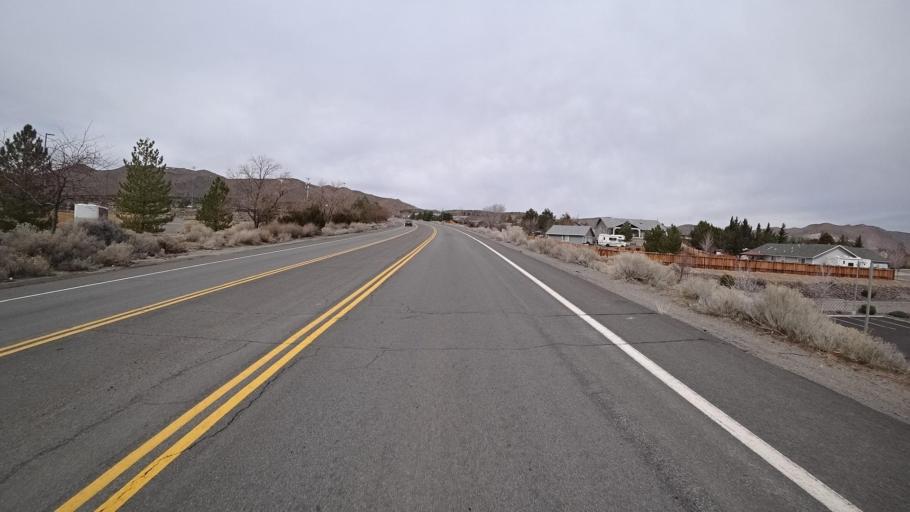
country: US
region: Nevada
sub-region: Washoe County
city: Spanish Springs
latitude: 39.6513
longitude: -119.7285
